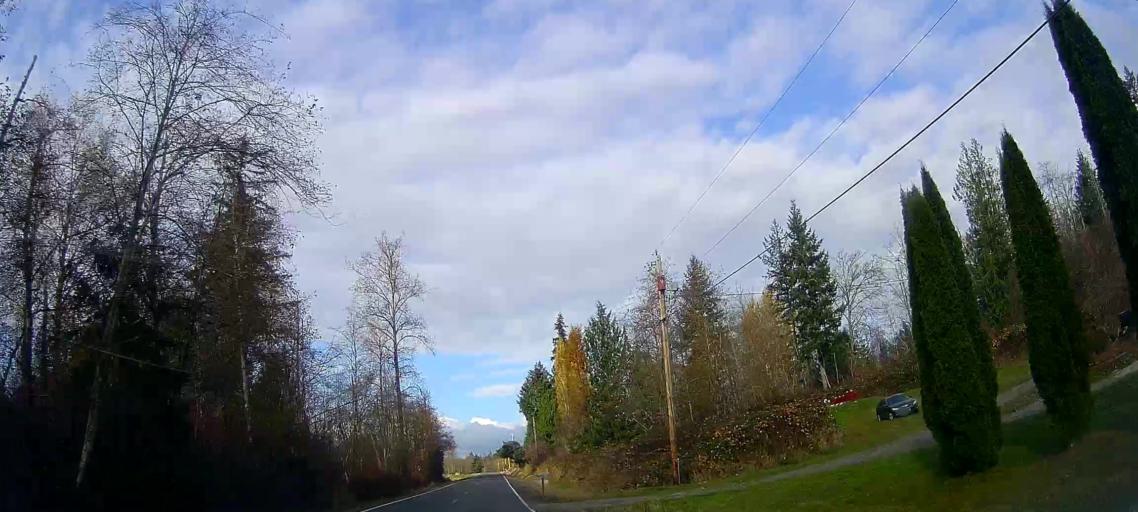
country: US
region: Washington
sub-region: Skagit County
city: Big Lake
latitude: 48.4195
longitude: -122.2362
